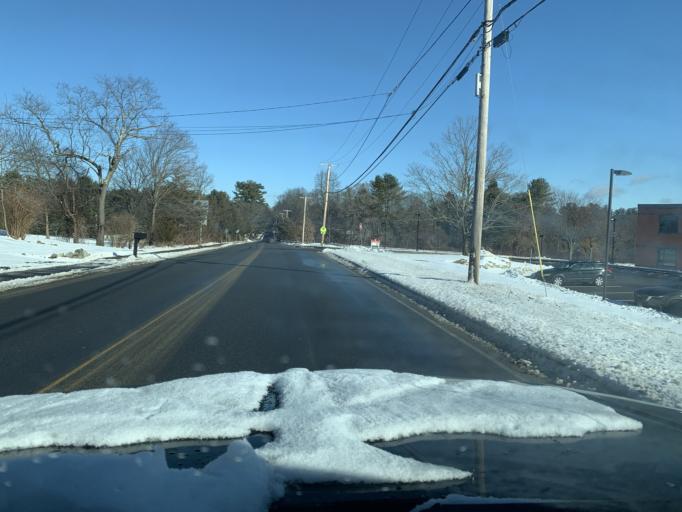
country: US
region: Massachusetts
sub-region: Essex County
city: Topsfield
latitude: 42.6278
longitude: -70.9765
